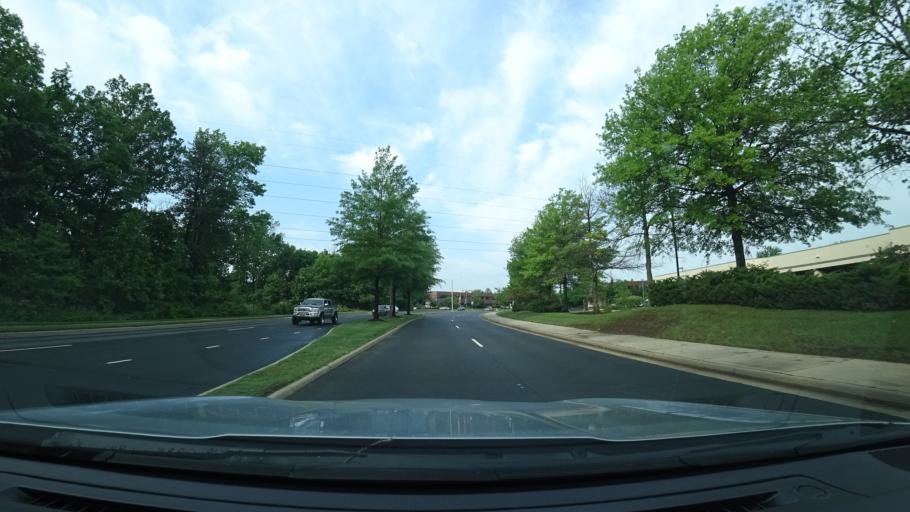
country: US
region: Virginia
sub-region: Fairfax County
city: Herndon
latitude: 38.9557
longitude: -77.3789
